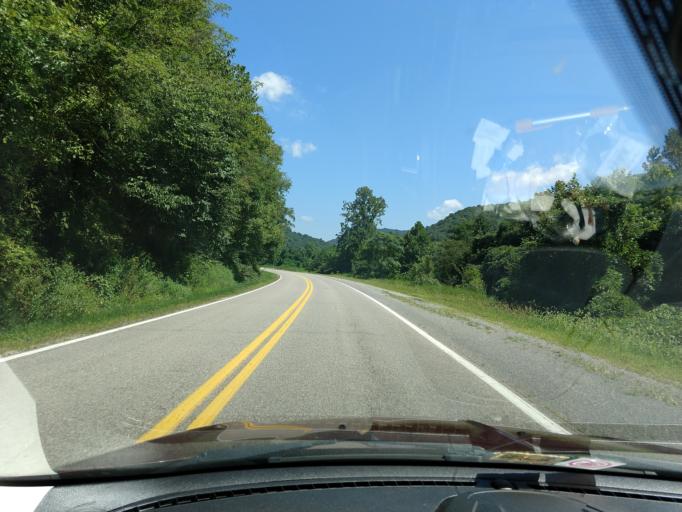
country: US
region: West Virginia
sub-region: Kanawha County
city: Montgomery
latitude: 38.1264
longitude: -81.2215
